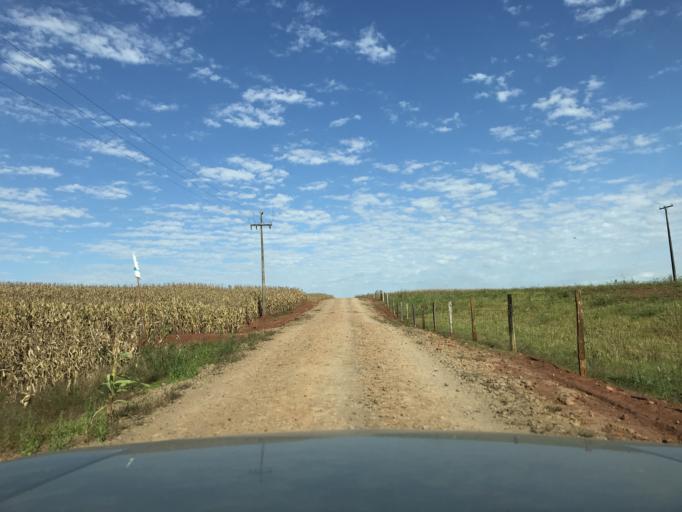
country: BR
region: Parana
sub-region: Palotina
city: Palotina
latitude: -24.1674
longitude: -53.7541
